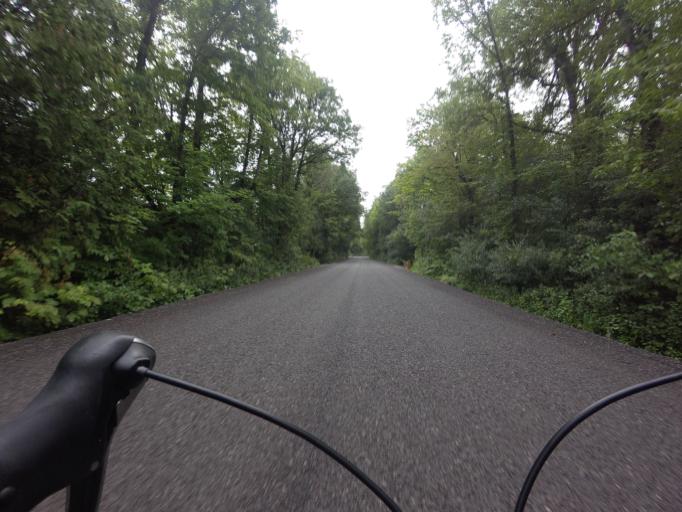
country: CA
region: Ontario
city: Bells Corners
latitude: 45.0734
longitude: -75.7570
